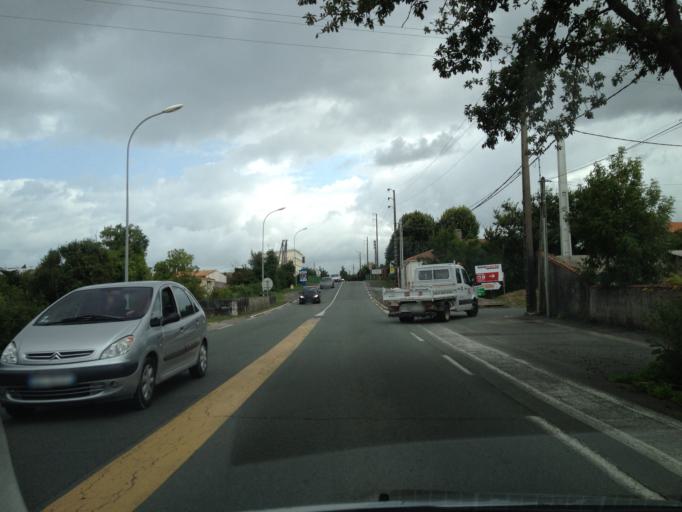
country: FR
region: Poitou-Charentes
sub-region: Departement de la Charente-Maritime
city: Marans
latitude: 46.3007
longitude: -0.9902
